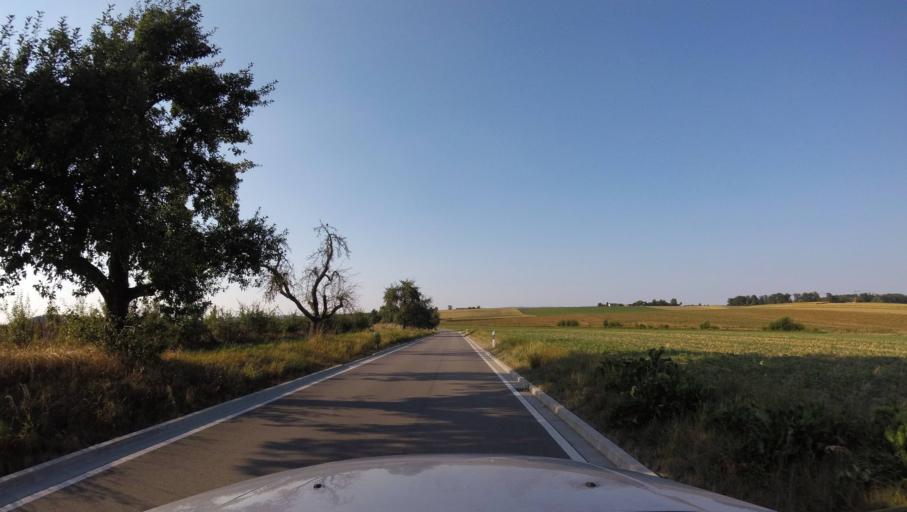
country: DE
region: Baden-Wuerttemberg
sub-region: Regierungsbezirk Stuttgart
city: Leutenbach
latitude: 48.9115
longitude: 9.4010
